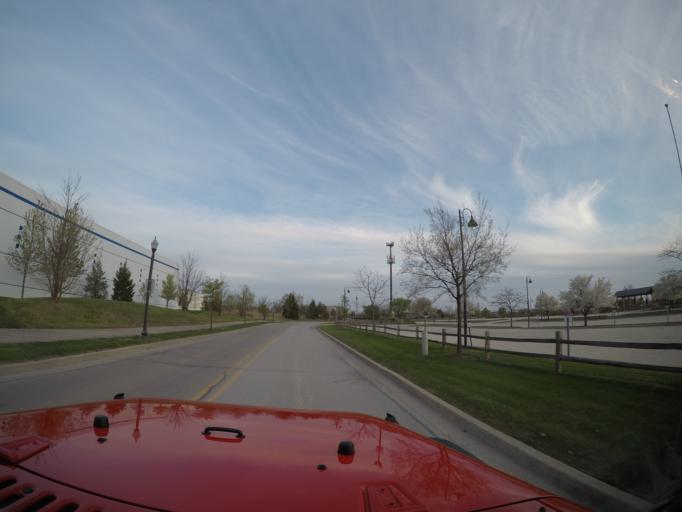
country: US
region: Illinois
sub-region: Cook County
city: Northfield
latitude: 42.0968
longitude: -87.8145
